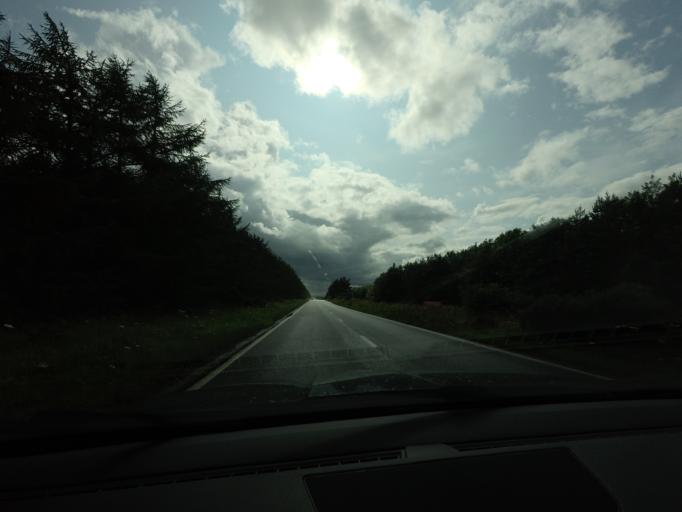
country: GB
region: Scotland
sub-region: Highland
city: Nairn
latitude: 57.5668
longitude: -3.9449
